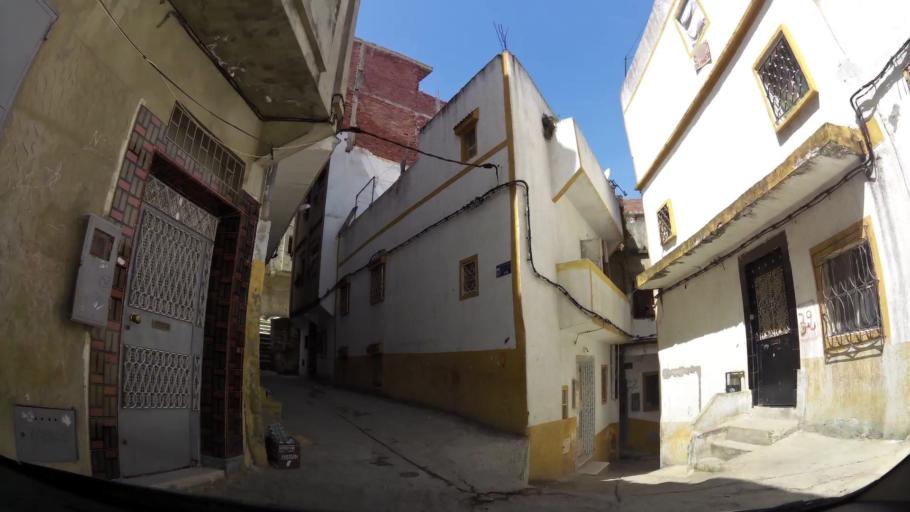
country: MA
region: Tanger-Tetouan
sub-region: Tanger-Assilah
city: Tangier
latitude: 35.7352
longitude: -5.8076
